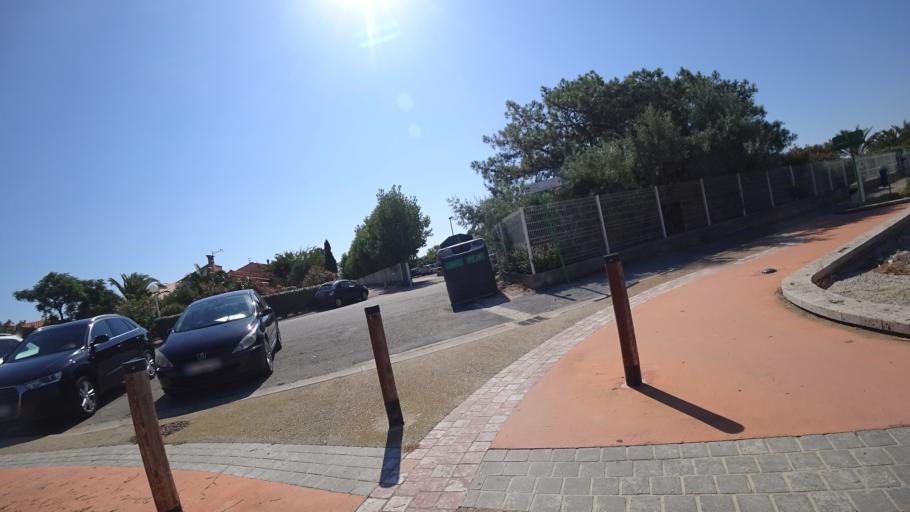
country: FR
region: Languedoc-Roussillon
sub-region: Departement des Pyrenees-Orientales
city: Le Barcares
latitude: 42.8059
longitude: 3.0329
